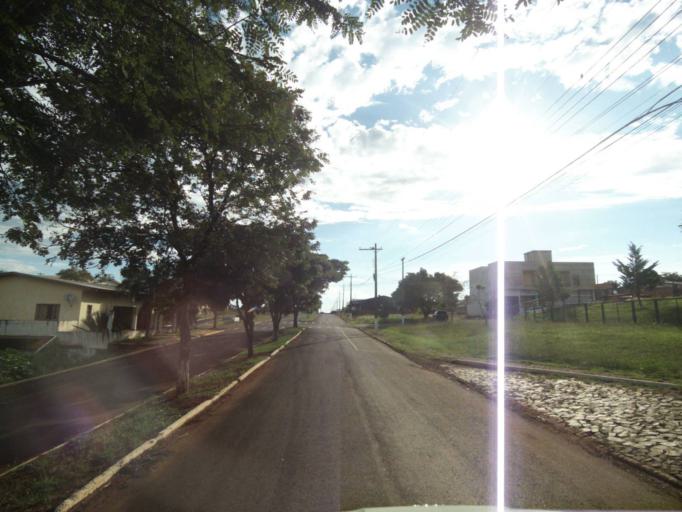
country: BR
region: Parana
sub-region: Laranjeiras Do Sul
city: Laranjeiras do Sul
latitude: -25.4938
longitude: -52.5319
